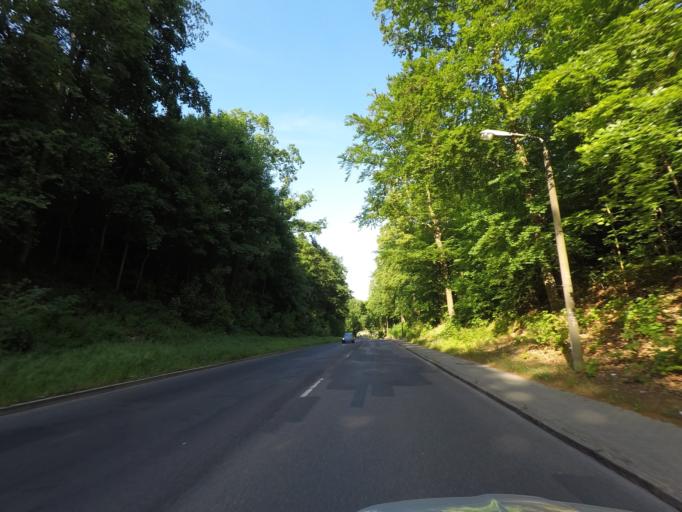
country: DE
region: Brandenburg
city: Bad Freienwalde
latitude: 52.7773
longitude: 14.0152
